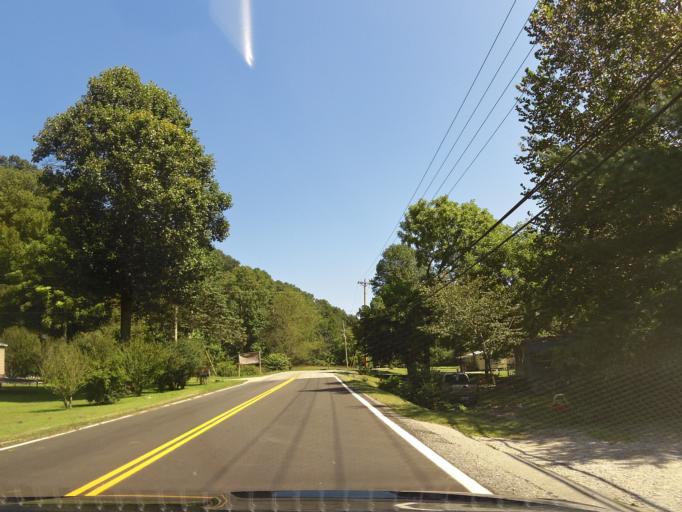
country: US
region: Kentucky
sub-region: Clay County
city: Manchester
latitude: 37.1306
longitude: -83.6223
